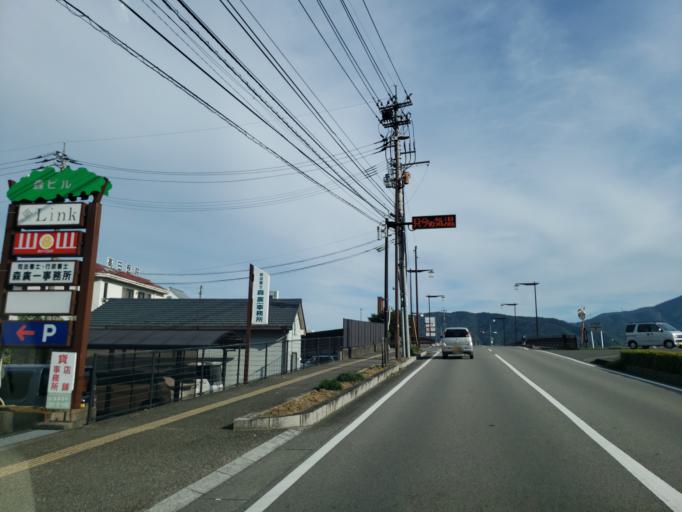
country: JP
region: Tokushima
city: Wakimachi
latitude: 34.0664
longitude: 134.1476
